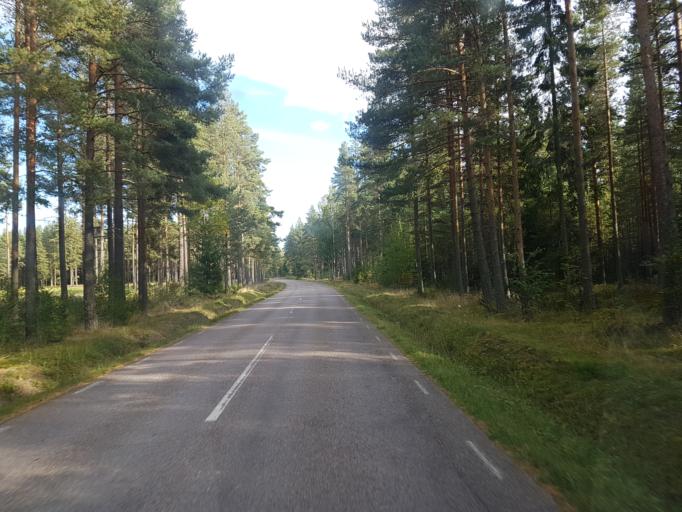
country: SE
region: Dalarna
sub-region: Saters Kommun
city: Saeter
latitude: 60.3923
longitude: 15.6541
